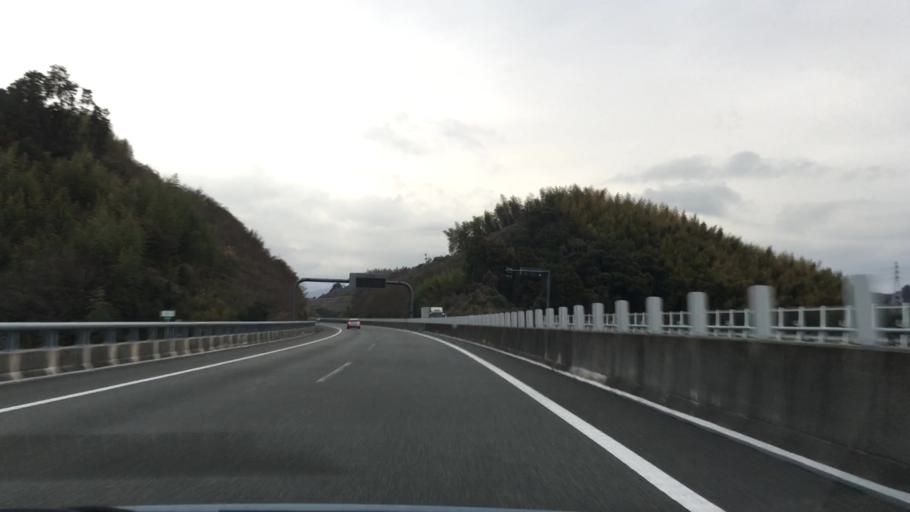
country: JP
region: Shizuoka
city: Shizuoka-shi
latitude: 35.0640
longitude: 138.4809
